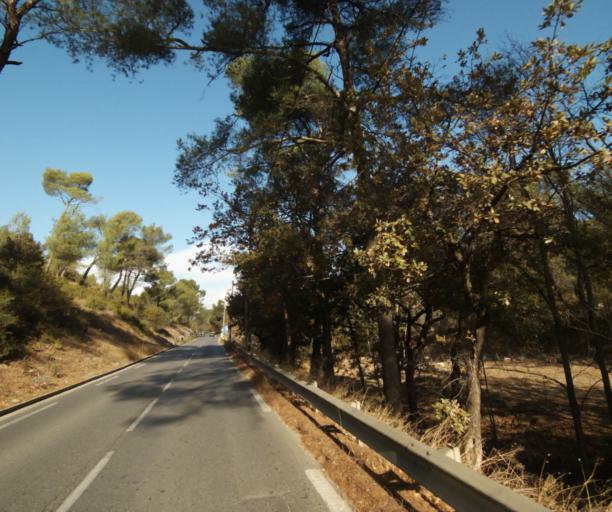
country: FR
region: Provence-Alpes-Cote d'Azur
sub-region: Departement des Bouches-du-Rhone
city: Allauch
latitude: 43.3143
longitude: 5.4984
